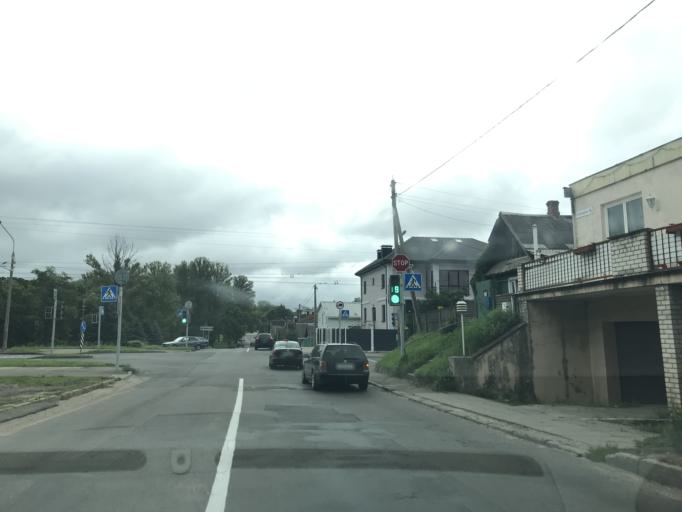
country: BY
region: Minsk
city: Minsk
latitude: 53.9401
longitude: 27.6163
